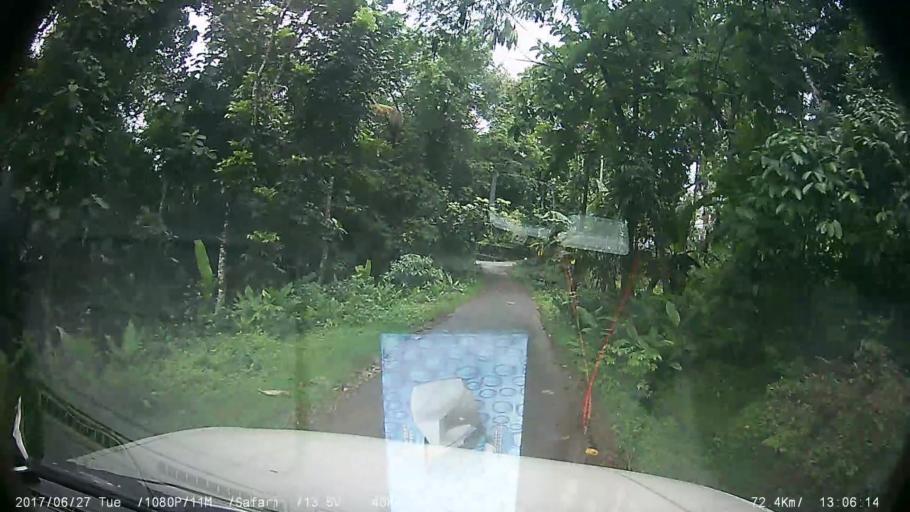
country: IN
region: Kerala
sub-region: Kottayam
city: Palackattumala
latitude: 9.7825
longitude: 76.5523
